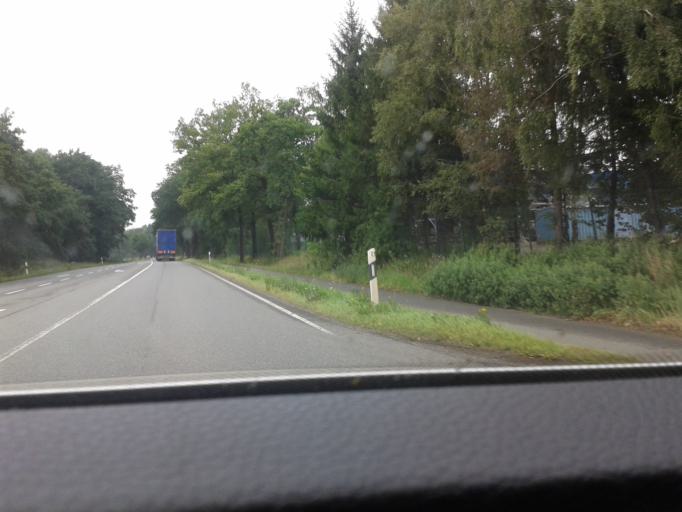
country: DE
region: Lower Saxony
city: Osloss
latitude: 52.4765
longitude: 10.6570
